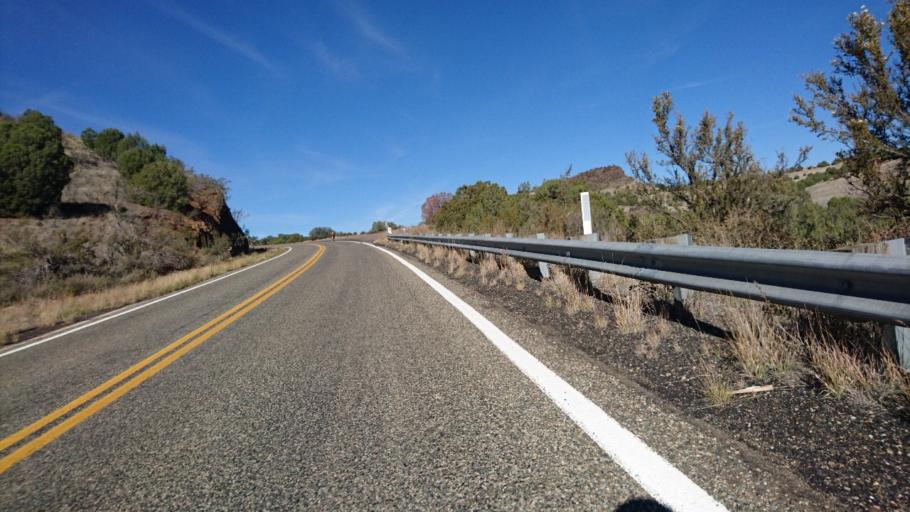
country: US
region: Arizona
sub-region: Yavapai County
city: Paulden
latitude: 35.2769
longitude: -112.6913
